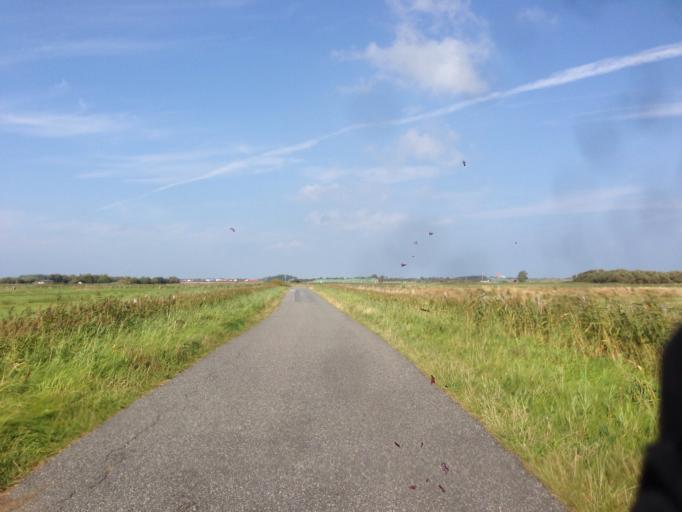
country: DE
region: Schleswig-Holstein
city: Tinnum
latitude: 54.8844
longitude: 8.3428
